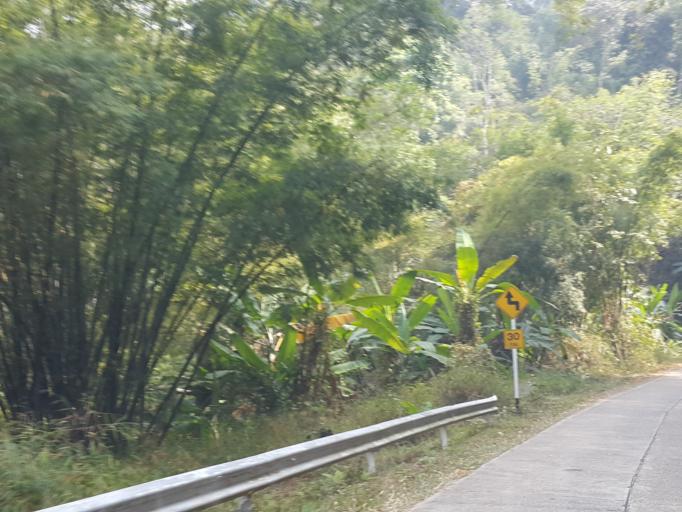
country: TH
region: Chiang Mai
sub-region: Amphoe Chiang Dao
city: Chiang Dao
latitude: 19.4124
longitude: 98.8683
